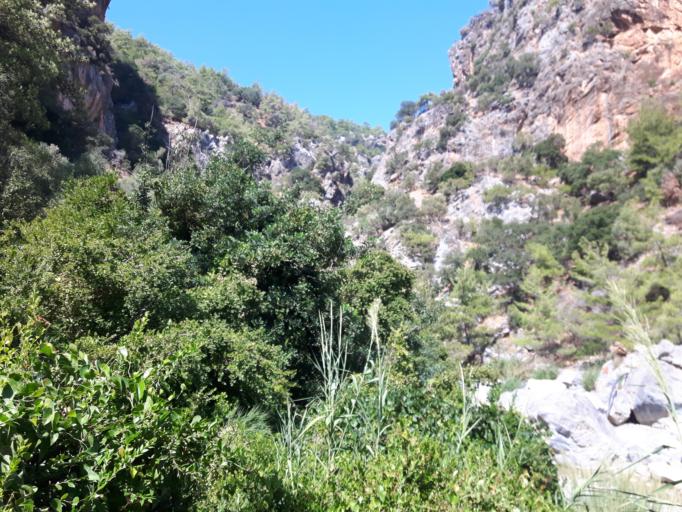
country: GR
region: Crete
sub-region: Nomos Lasithiou
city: Gra Liyia
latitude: 35.0482
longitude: 25.5784
